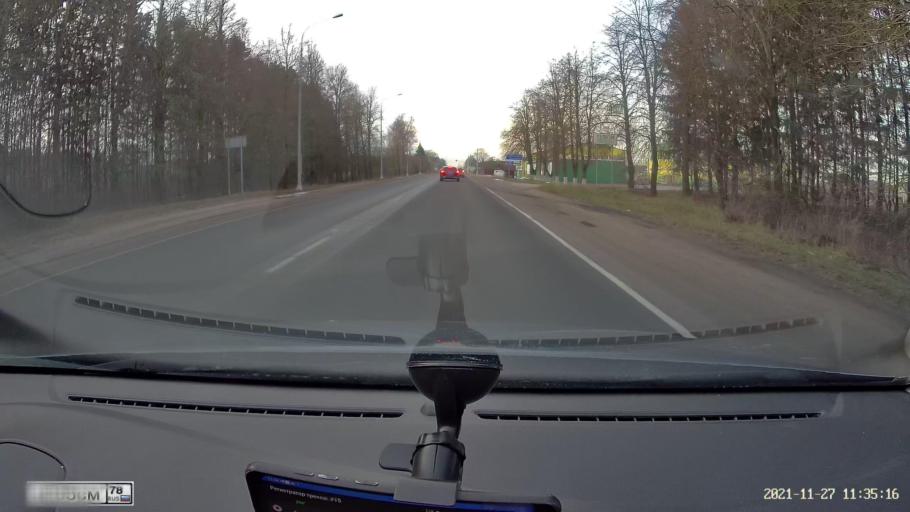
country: RU
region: Leningrad
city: Russko-Vysotskoye
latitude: 59.7029
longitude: 29.9843
